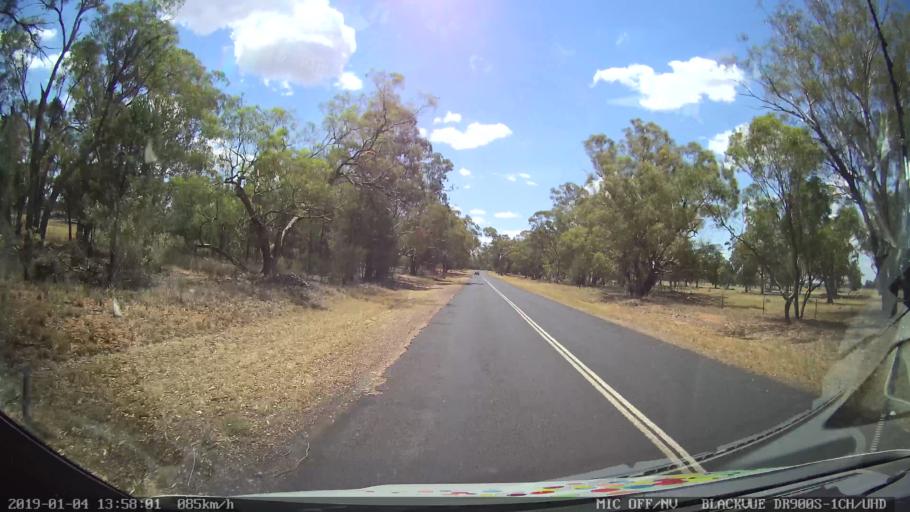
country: AU
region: New South Wales
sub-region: Dubbo Municipality
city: Dubbo
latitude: -32.3338
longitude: 148.5954
